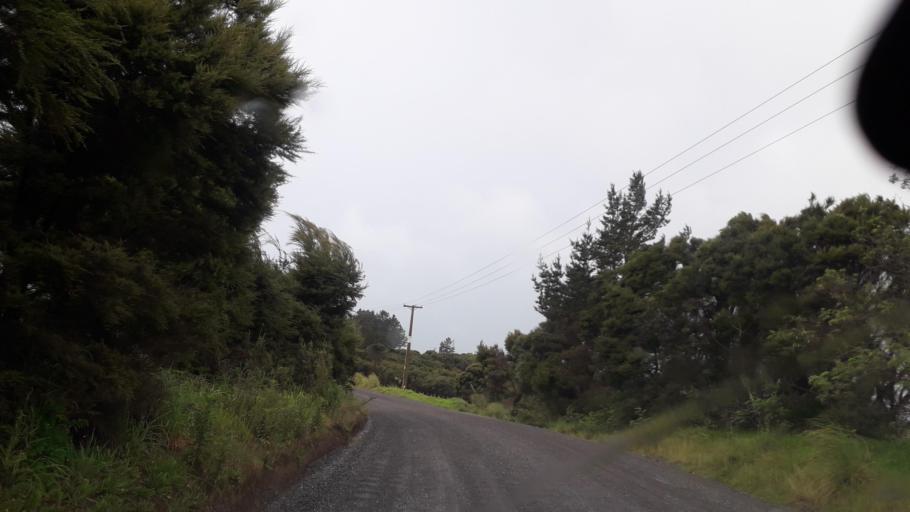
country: NZ
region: Northland
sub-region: Far North District
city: Kerikeri
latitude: -35.1370
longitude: 173.9982
